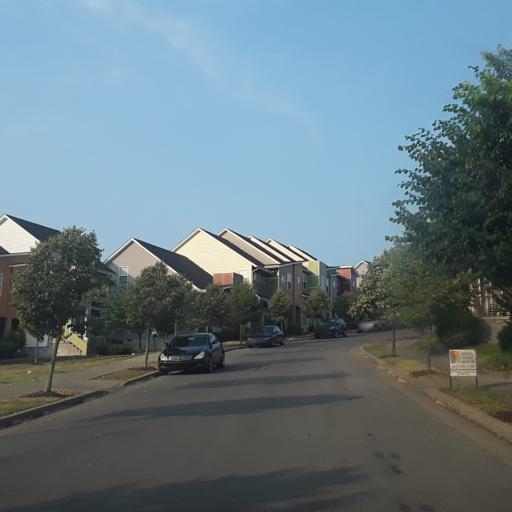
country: US
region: Tennessee
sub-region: Williamson County
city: Brentwood Estates
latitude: 36.0414
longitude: -86.7226
